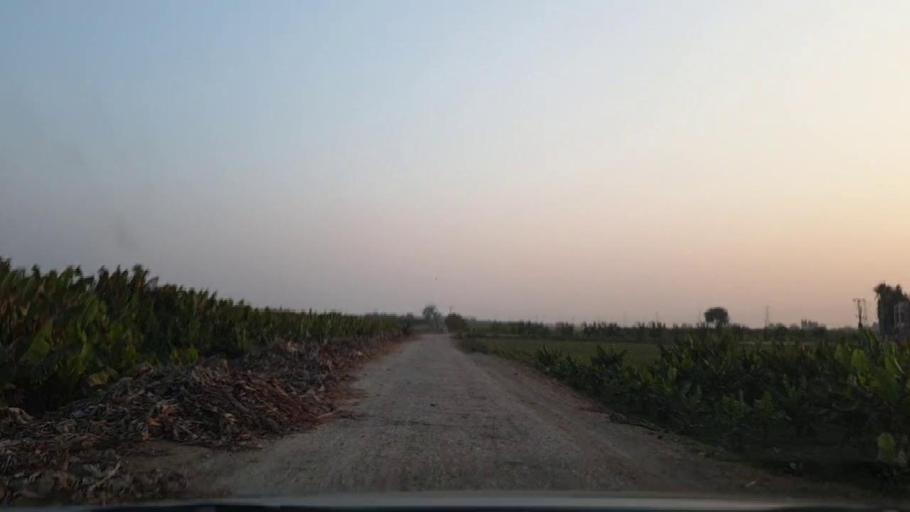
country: PK
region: Sindh
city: Matiari
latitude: 25.6790
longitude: 68.5241
